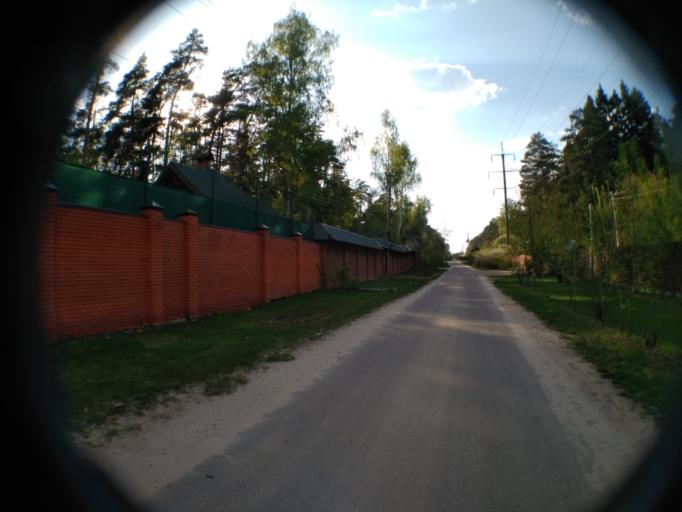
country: RU
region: Moskovskaya
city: Kratovo
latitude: 55.5791
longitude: 38.1679
